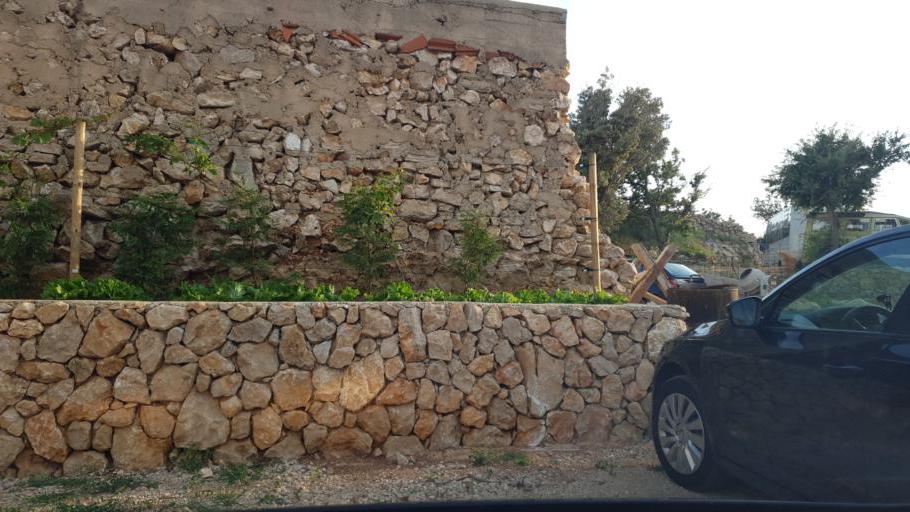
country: HR
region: Primorsko-Goranska
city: Punat
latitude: 44.9523
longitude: 14.6905
